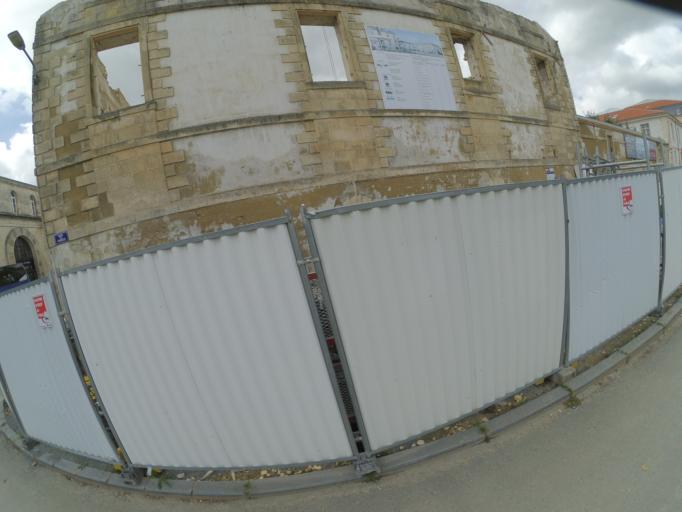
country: FR
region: Poitou-Charentes
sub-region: Departement de la Charente-Maritime
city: Rochefort
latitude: 45.9417
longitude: -0.9566
